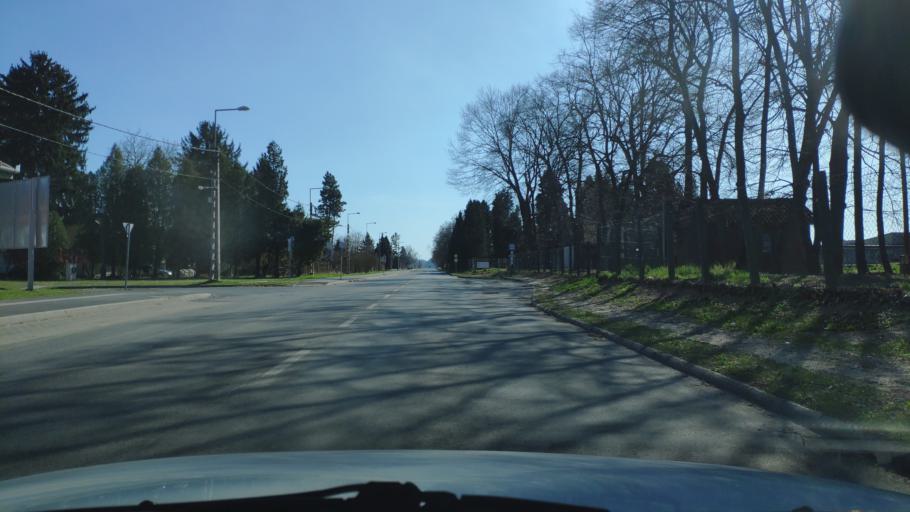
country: HU
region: Zala
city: Nagykanizsa
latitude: 46.4284
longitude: 16.9868
